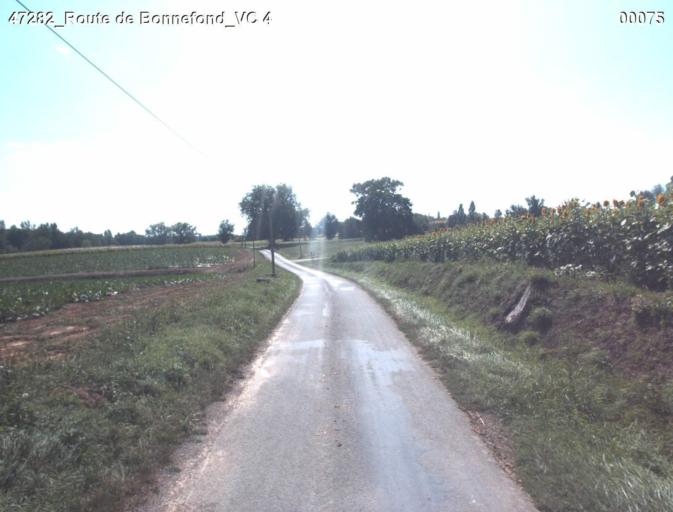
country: FR
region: Aquitaine
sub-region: Departement du Lot-et-Garonne
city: Laplume
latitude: 44.1054
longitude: 0.4755
